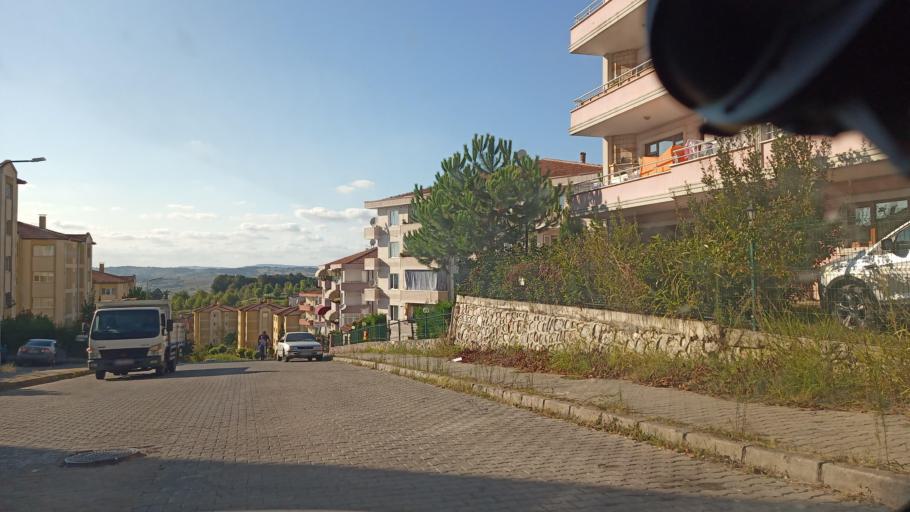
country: TR
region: Kocaeli
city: Kaymaz
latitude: 40.8606
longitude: 30.2912
